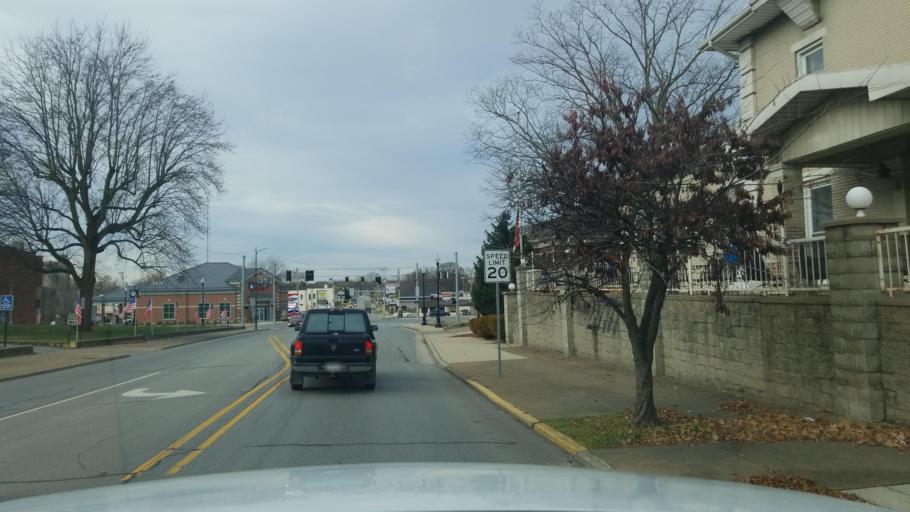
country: US
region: Indiana
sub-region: Posey County
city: Mount Vernon
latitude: 37.9325
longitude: -87.8945
